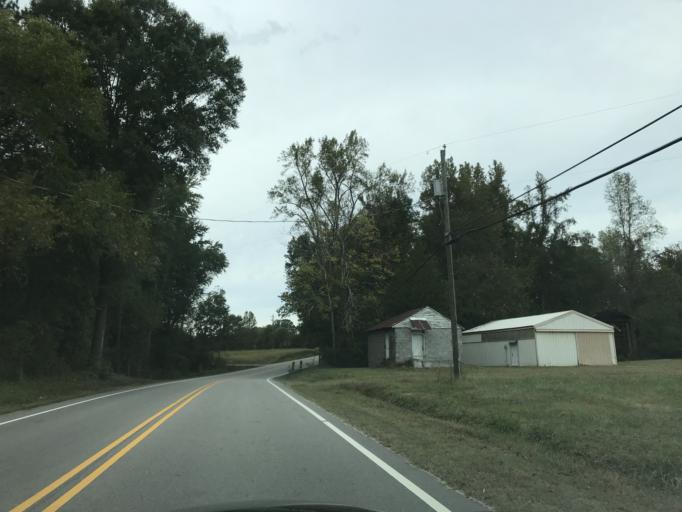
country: US
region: North Carolina
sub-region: Wake County
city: Knightdale
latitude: 35.8224
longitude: -78.5041
